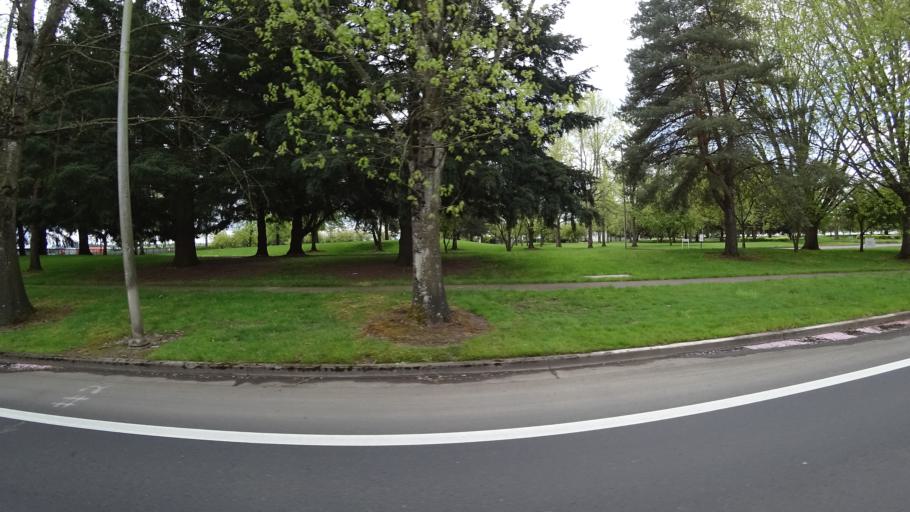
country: US
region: Oregon
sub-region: Washington County
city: Rockcreek
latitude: 45.5466
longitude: -122.9044
